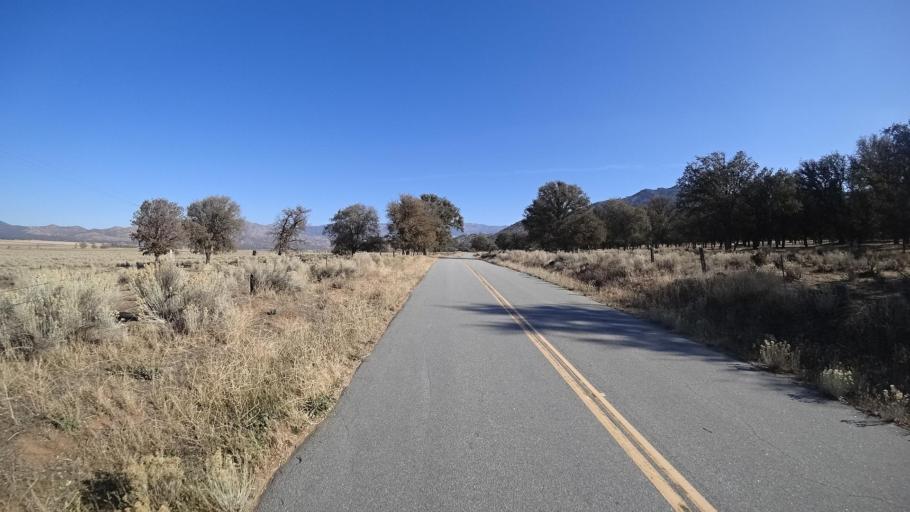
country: US
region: California
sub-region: Kern County
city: Bodfish
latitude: 35.3824
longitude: -118.5440
